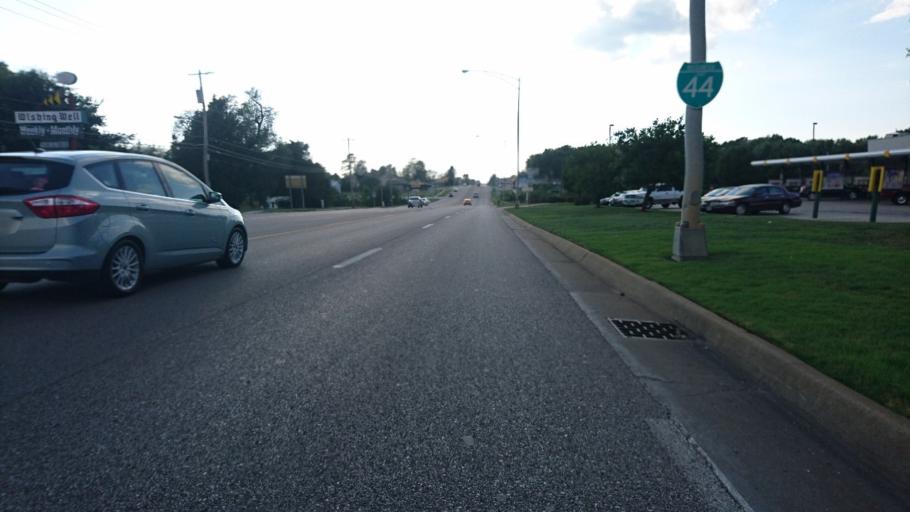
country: US
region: Missouri
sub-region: Greene County
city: Springfield
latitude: 37.2123
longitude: -93.3500
